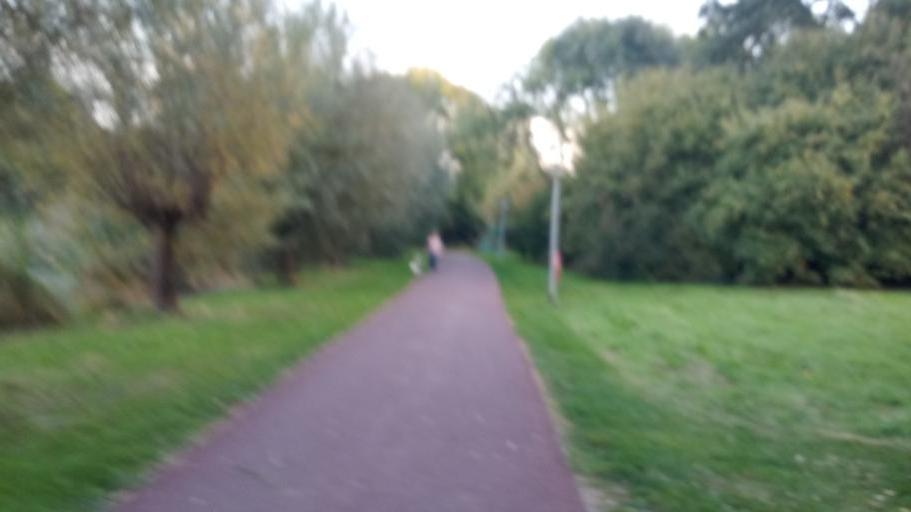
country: NL
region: Gelderland
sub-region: Gemeente Zutphen
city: Zutphen
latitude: 52.1284
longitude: 6.2028
